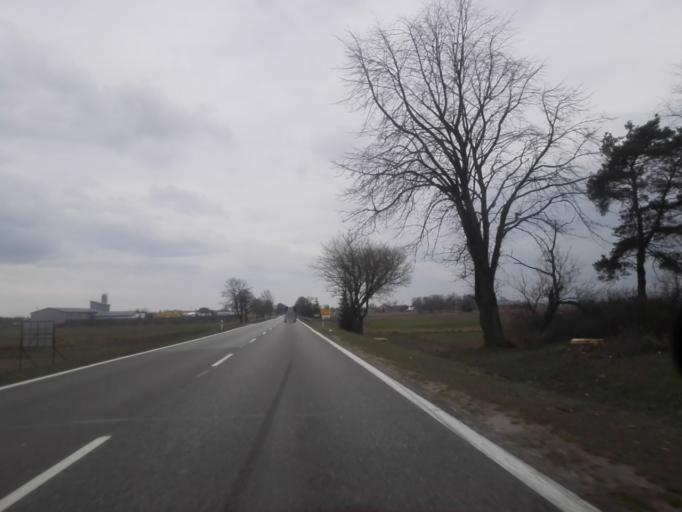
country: PL
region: Podlasie
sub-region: Powiat augustowski
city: Augustow
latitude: 53.8238
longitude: 22.9416
